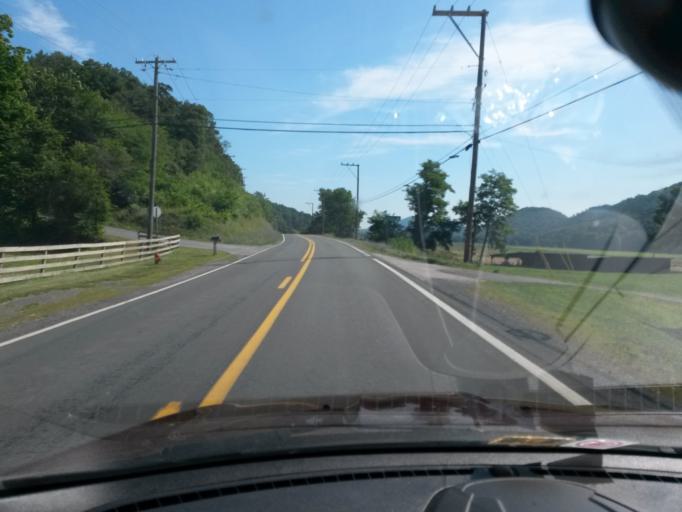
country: US
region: West Virginia
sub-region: Hardy County
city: Moorefield
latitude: 39.0186
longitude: -78.7628
